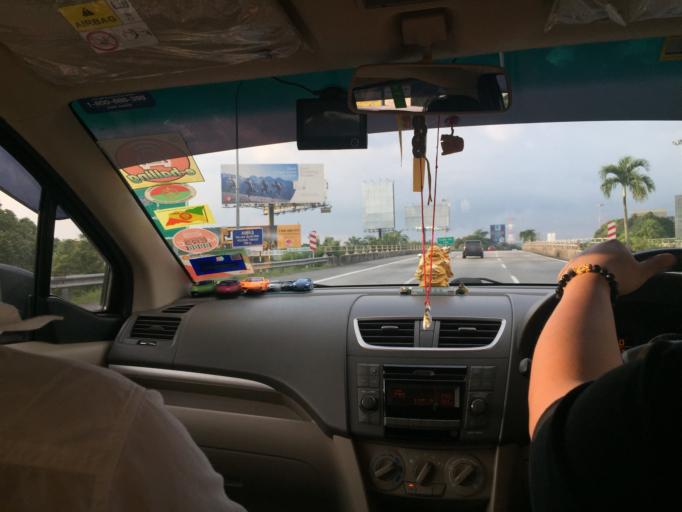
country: MY
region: Putrajaya
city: Putrajaya
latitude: 2.8229
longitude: 101.6611
